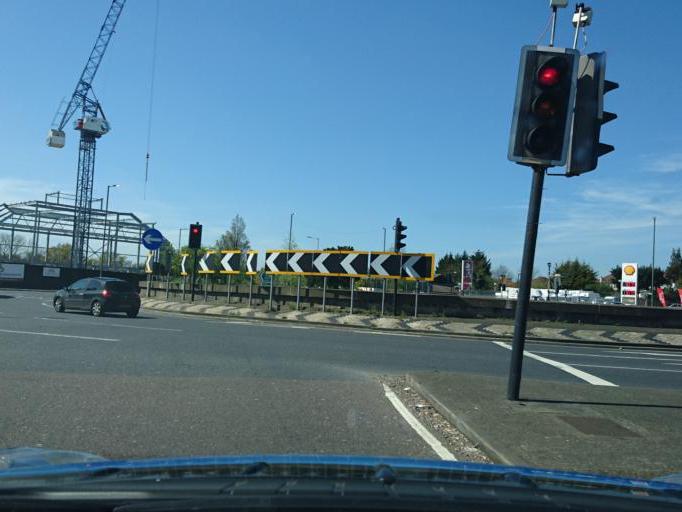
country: GB
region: England
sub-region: Greater London
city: Edgware
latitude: 51.6213
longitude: -0.2545
